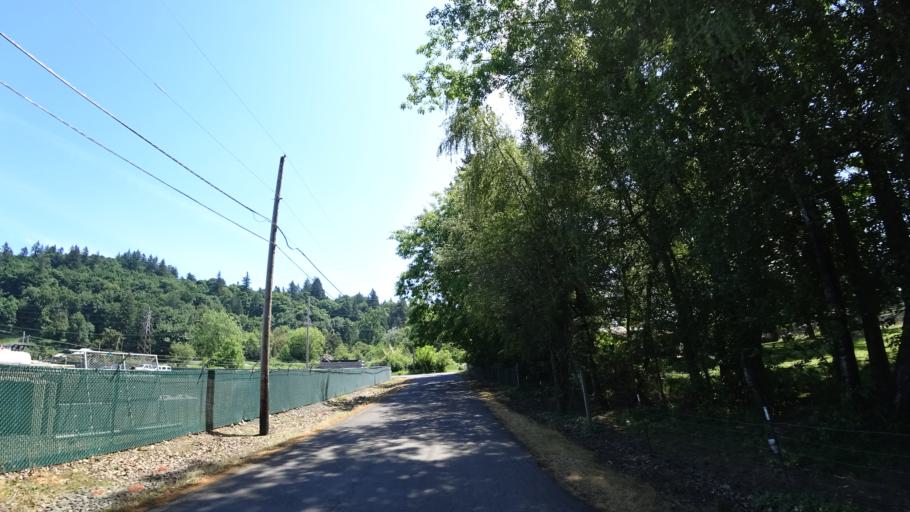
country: US
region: Oregon
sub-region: Multnomah County
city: Gresham
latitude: 45.4859
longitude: -122.4870
